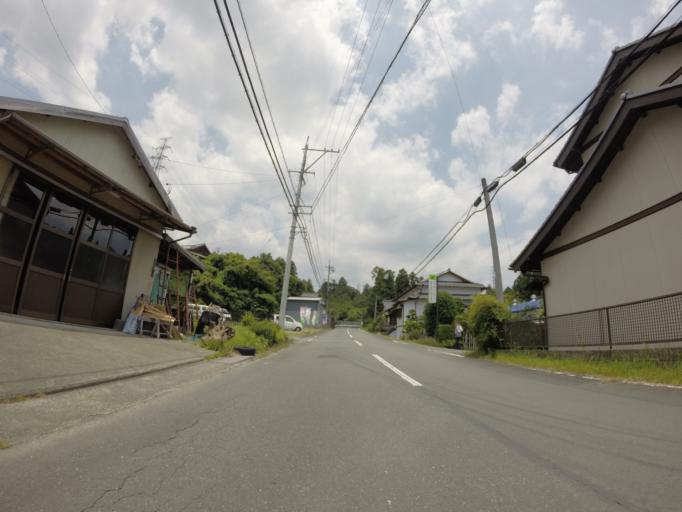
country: JP
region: Shizuoka
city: Kanaya
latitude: 34.8131
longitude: 138.0676
